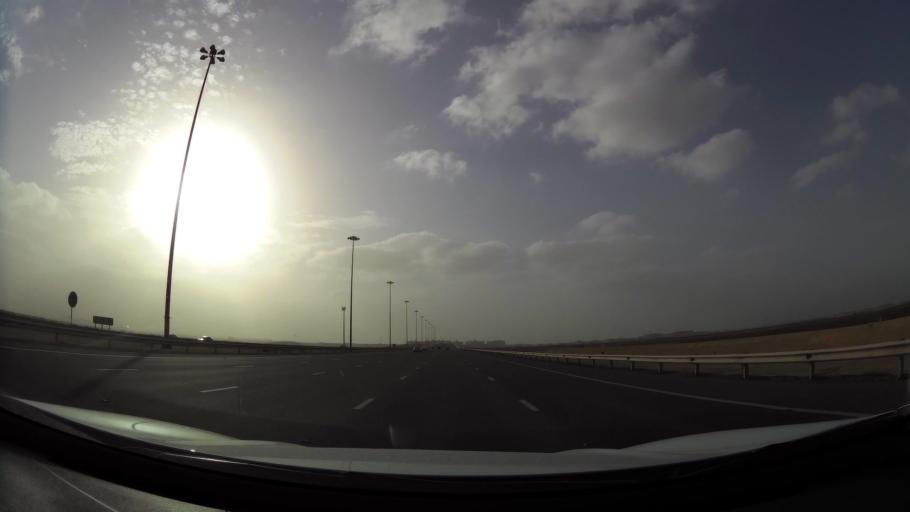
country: AE
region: Abu Dhabi
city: Abu Dhabi
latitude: 24.5476
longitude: 54.4690
